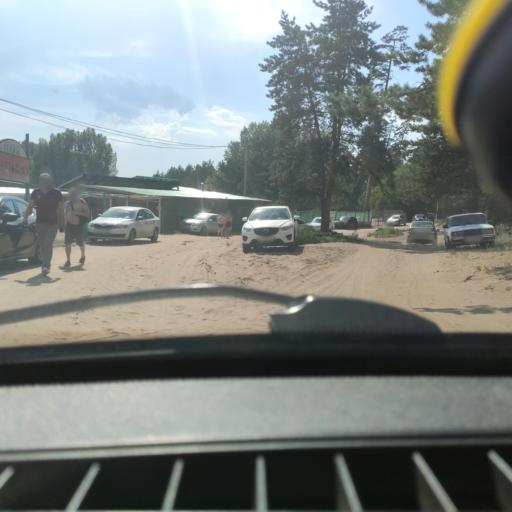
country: RU
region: Samara
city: Tol'yatti
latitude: 53.4738
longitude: 49.3362
